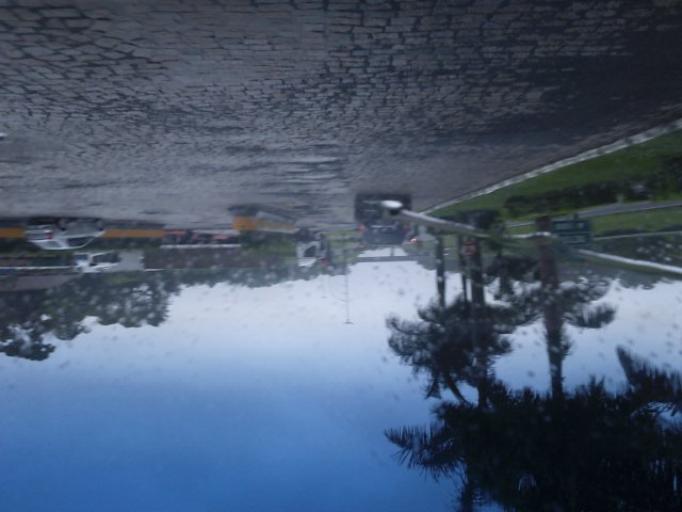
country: BR
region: Sao Paulo
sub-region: Pariquera-Acu
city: Pariquera Acu
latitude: -24.6227
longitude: -47.8954
